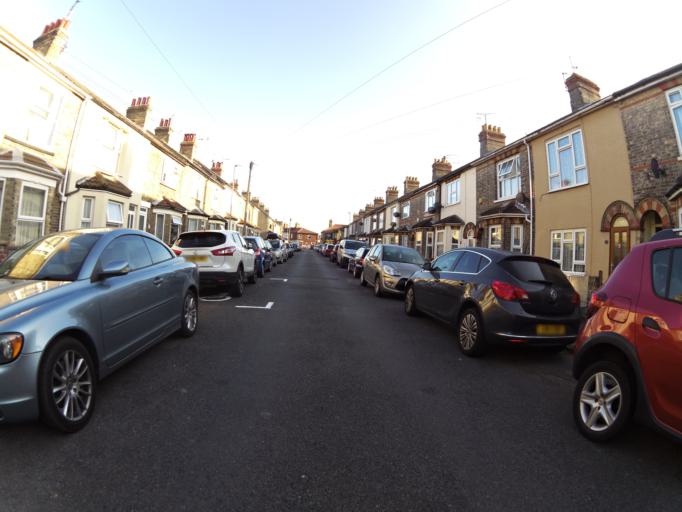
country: GB
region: England
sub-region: Suffolk
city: Lowestoft
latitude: 52.4678
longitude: 1.7389
